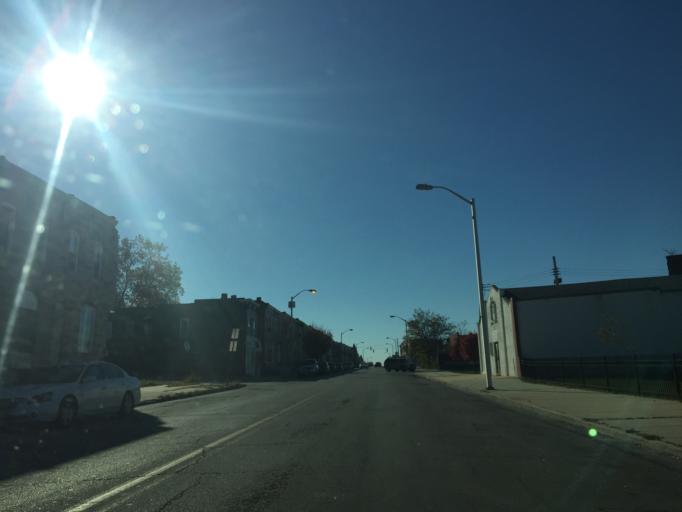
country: US
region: Maryland
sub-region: City of Baltimore
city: Baltimore
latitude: 39.3104
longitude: -76.5858
